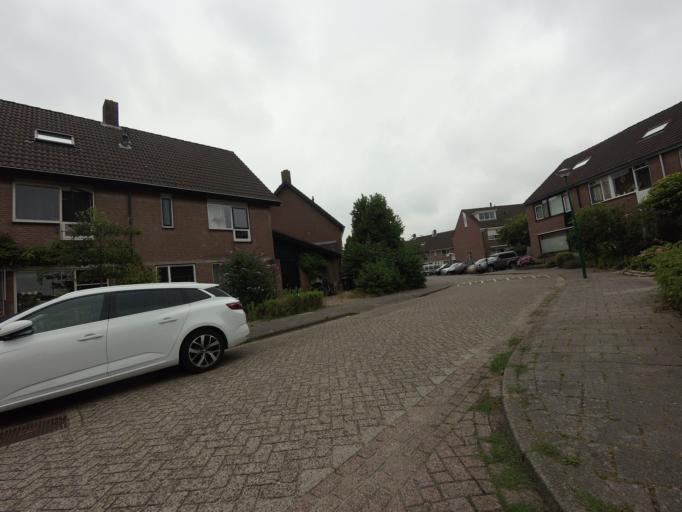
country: NL
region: Utrecht
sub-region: Gemeente Wijk bij Duurstede
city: Wijk bij Duurstede
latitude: 51.9820
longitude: 5.3474
